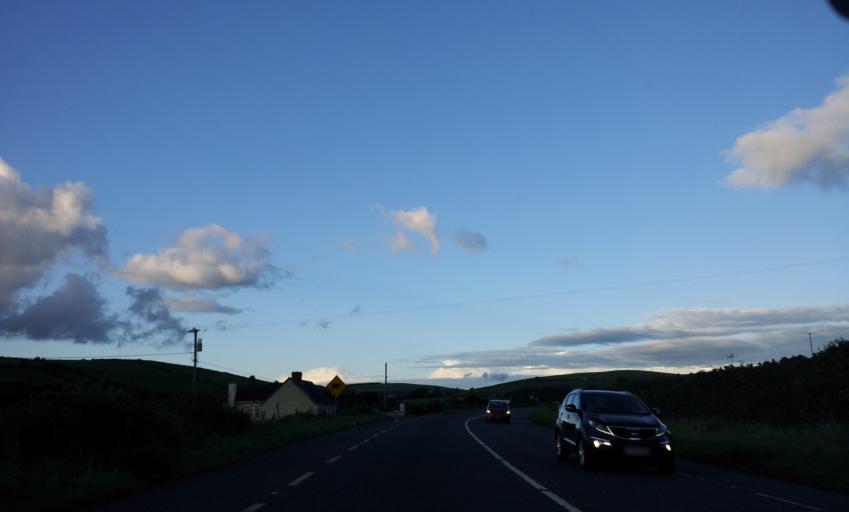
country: IE
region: Munster
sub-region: County Limerick
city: Newcastle West
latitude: 52.4063
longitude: -9.1668
